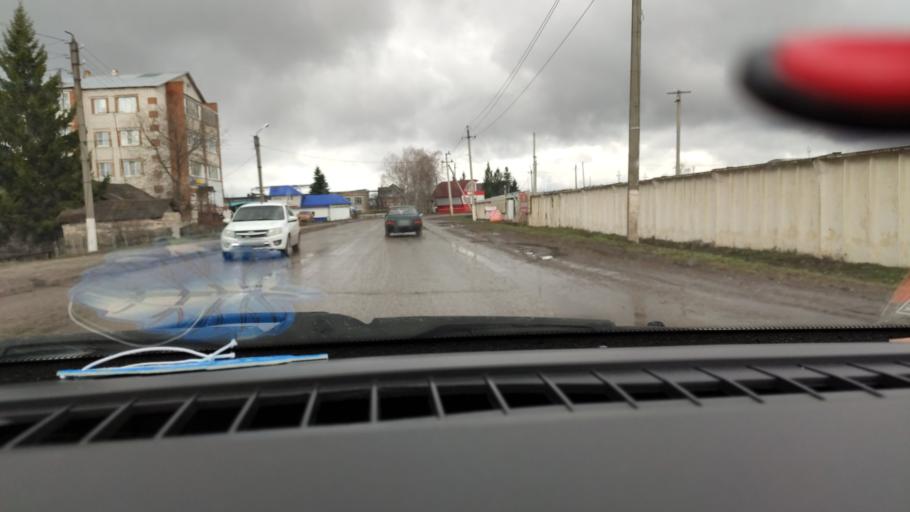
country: RU
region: Tatarstan
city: Nurlat
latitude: 54.4239
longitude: 50.7885
